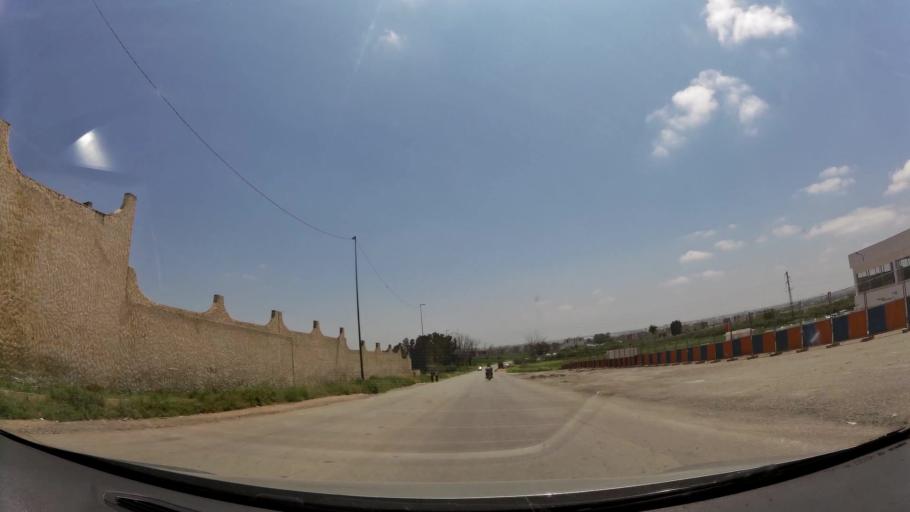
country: MA
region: Fes-Boulemane
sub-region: Fes
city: Fes
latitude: 34.0423
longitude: -5.0628
